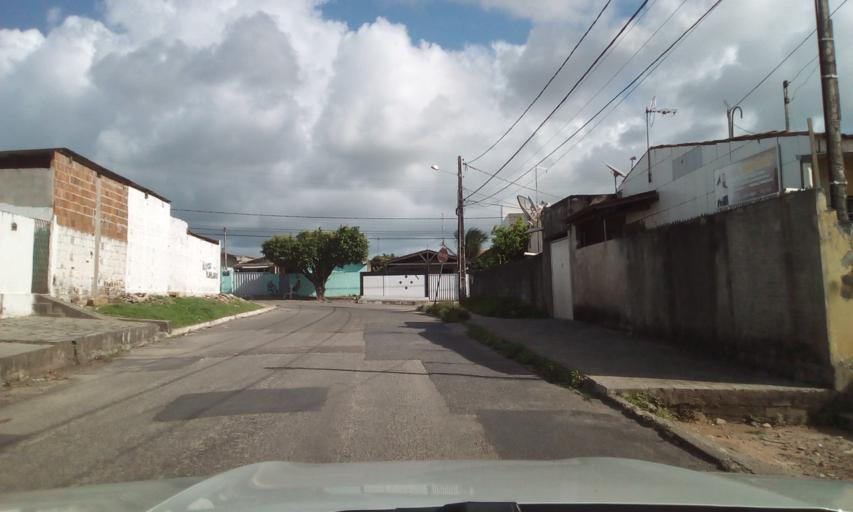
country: BR
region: Paraiba
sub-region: Joao Pessoa
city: Joao Pessoa
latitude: -7.1769
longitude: -34.8807
